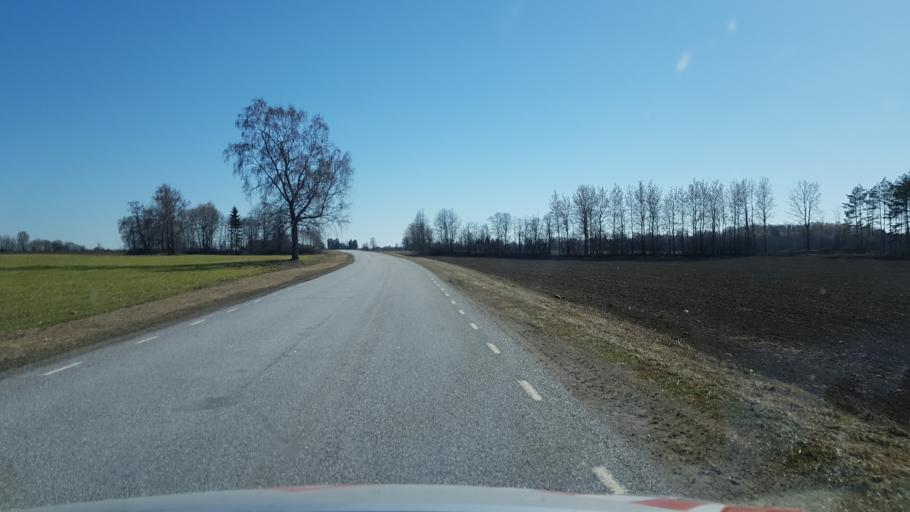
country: EE
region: Jaervamaa
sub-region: Koeru vald
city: Koeru
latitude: 59.0247
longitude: 26.0884
